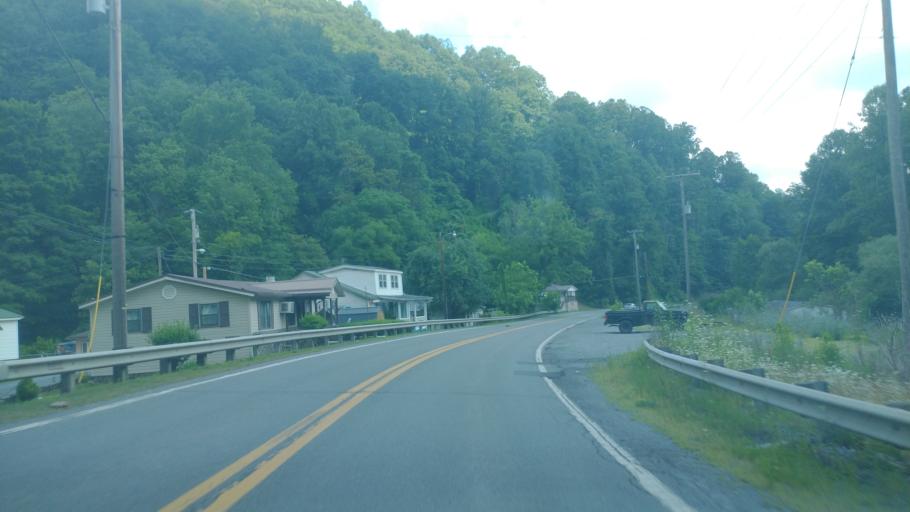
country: US
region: West Virginia
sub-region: McDowell County
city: Welch
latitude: 37.3886
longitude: -81.4211
